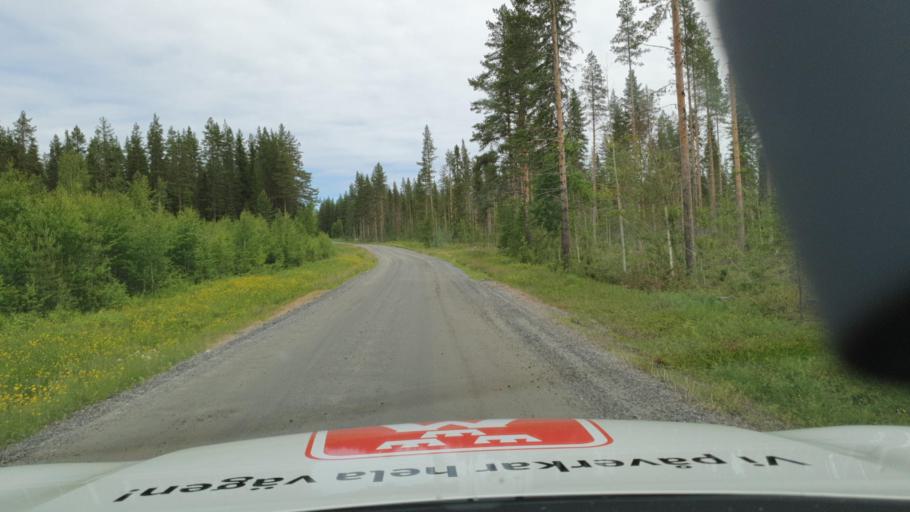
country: SE
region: Vaesterbotten
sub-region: Skelleftea Kommun
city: Forsbacka
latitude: 64.5209
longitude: 20.3259
